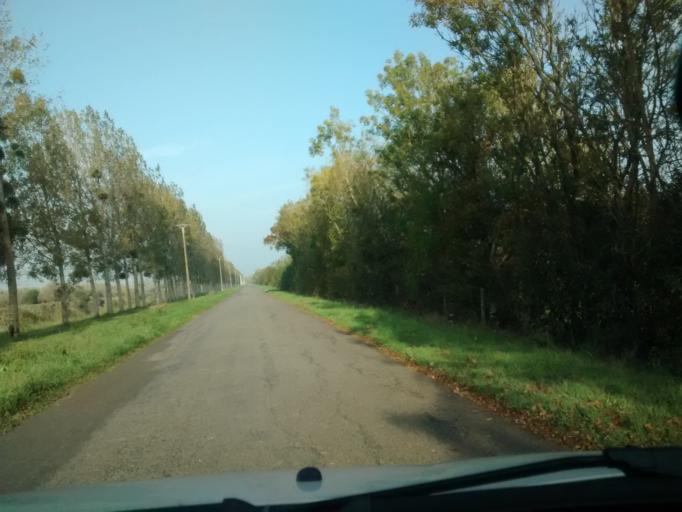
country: FR
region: Pays de la Loire
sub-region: Departement de la Loire-Atlantique
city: Vue
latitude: 47.2306
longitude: -1.8548
